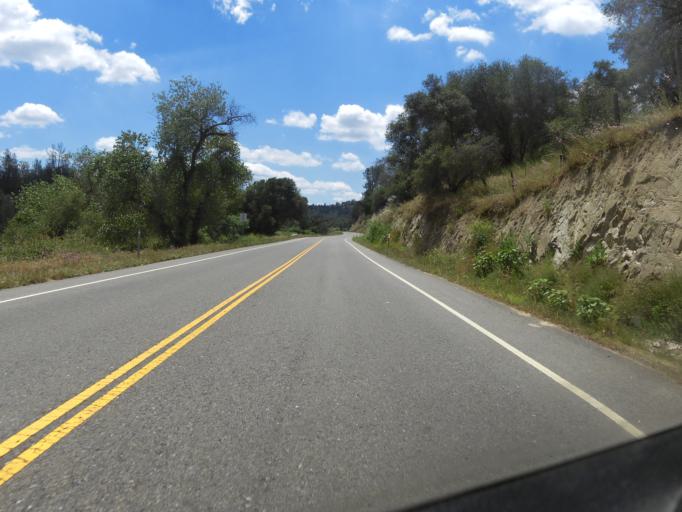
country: US
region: California
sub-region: Madera County
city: Coarsegold
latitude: 37.1657
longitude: -119.6403
